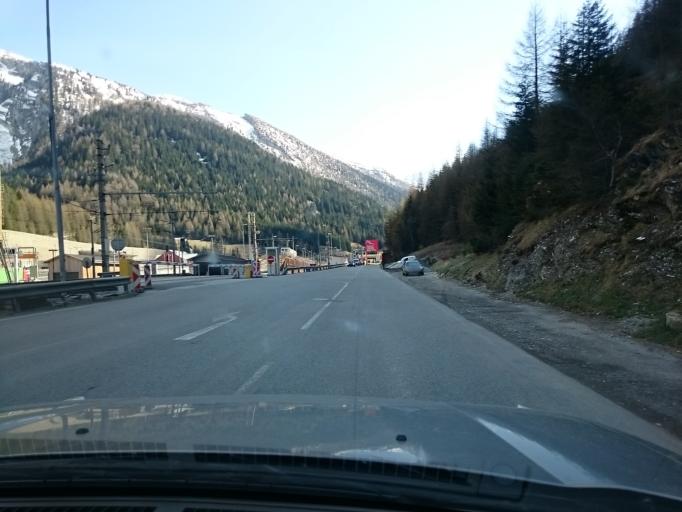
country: AT
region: Tyrol
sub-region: Politischer Bezirk Innsbruck Land
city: Gries am Brenner
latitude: 47.0113
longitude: 11.5070
